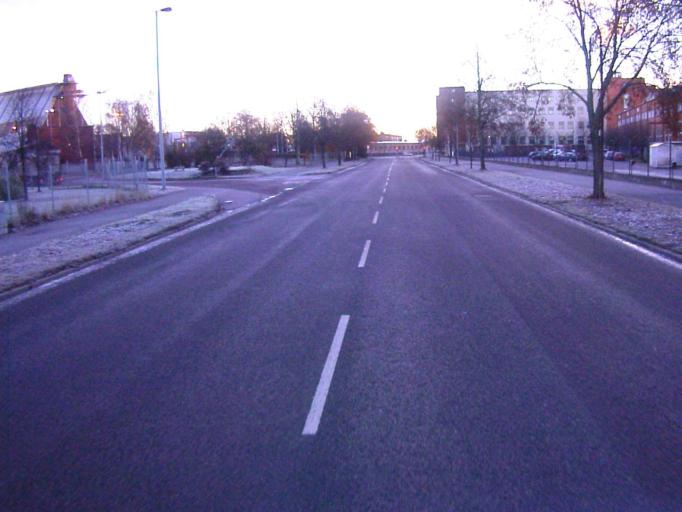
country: SE
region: Soedermanland
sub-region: Eskilstuna Kommun
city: Eskilstuna
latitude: 59.3798
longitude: 16.4919
